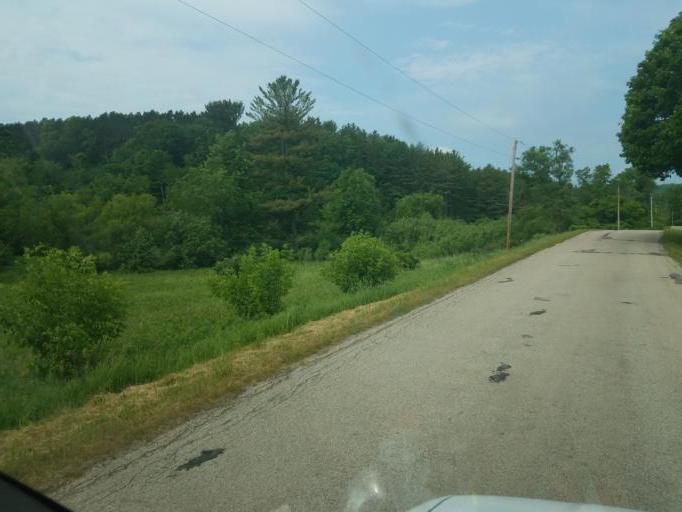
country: US
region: Wisconsin
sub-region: Monroe County
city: Cashton
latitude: 43.7105
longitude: -90.5751
